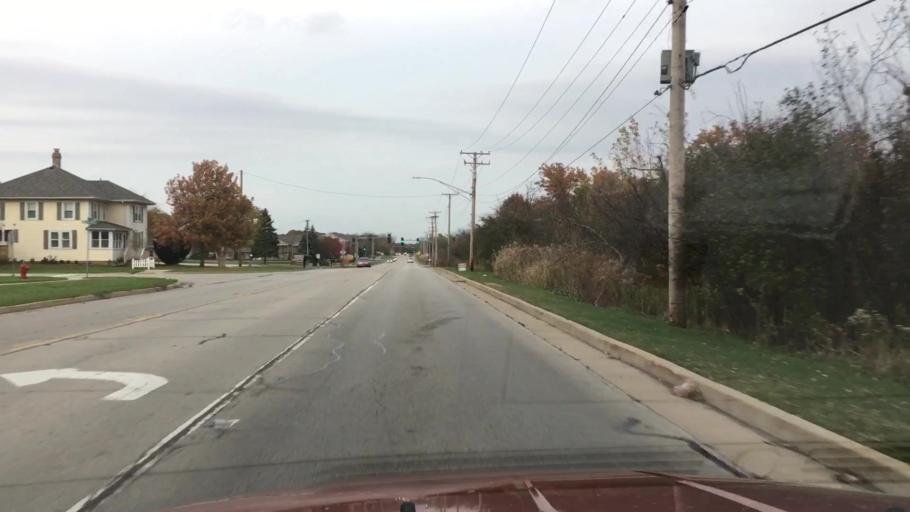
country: US
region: Illinois
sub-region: Cook County
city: Tinley Park
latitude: 41.6116
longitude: -87.7856
